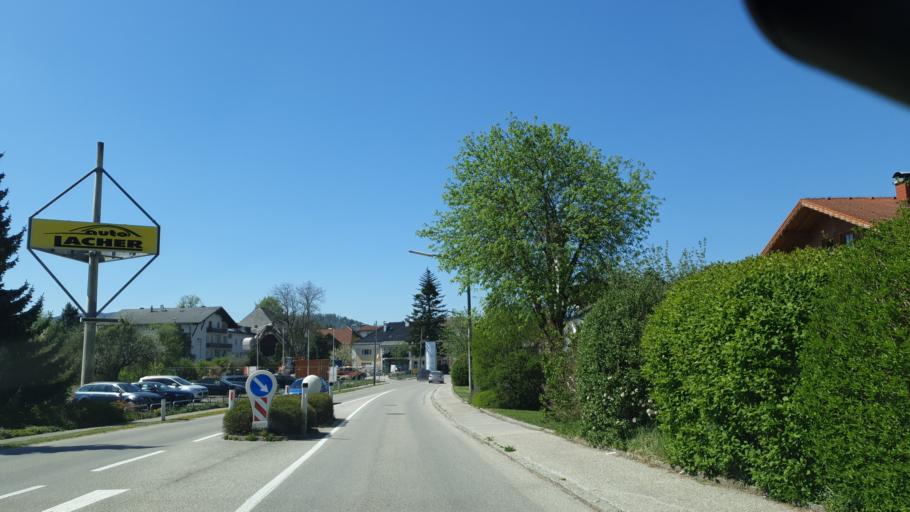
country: AT
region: Upper Austria
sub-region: Politischer Bezirk Vocklabruck
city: Sankt Georgen im Attergau
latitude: 47.9323
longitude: 13.4937
